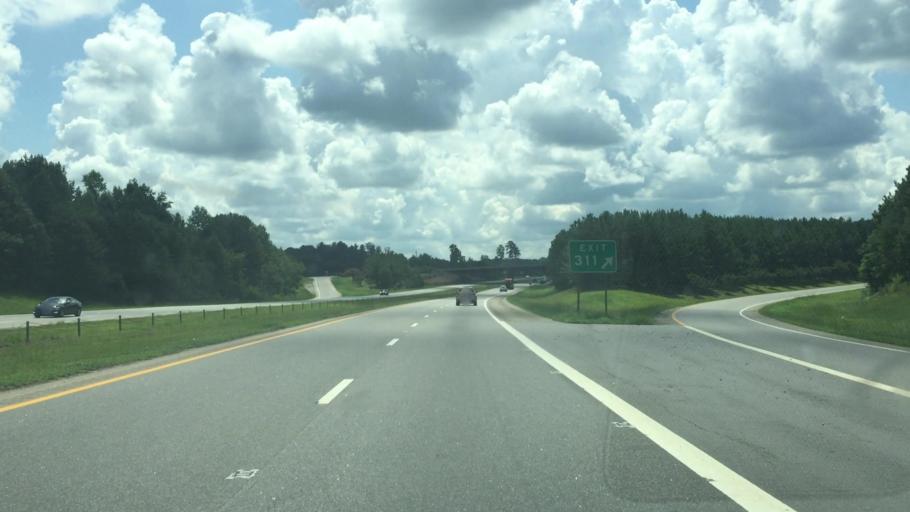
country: US
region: North Carolina
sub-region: Richmond County
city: Cordova
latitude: 34.9138
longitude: -79.7953
